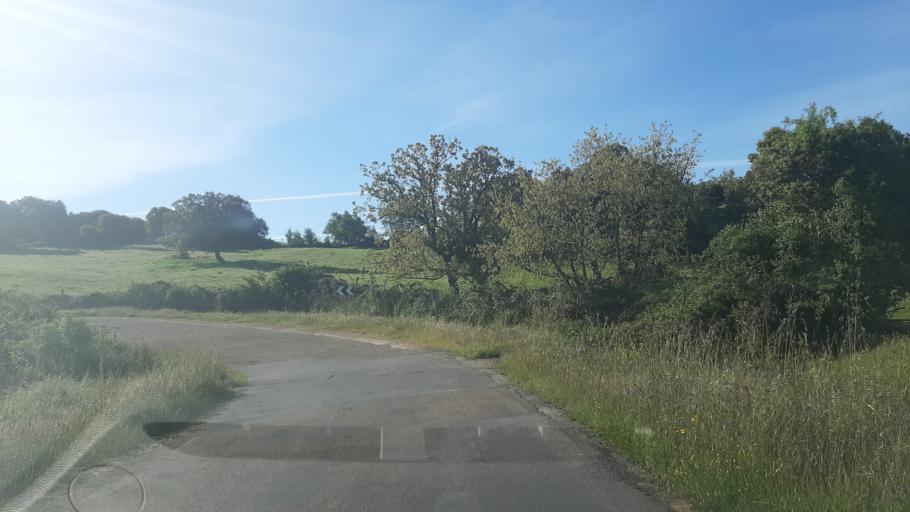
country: ES
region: Castille and Leon
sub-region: Provincia de Salamanca
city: Guijo de Avila
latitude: 40.5326
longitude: -5.6467
